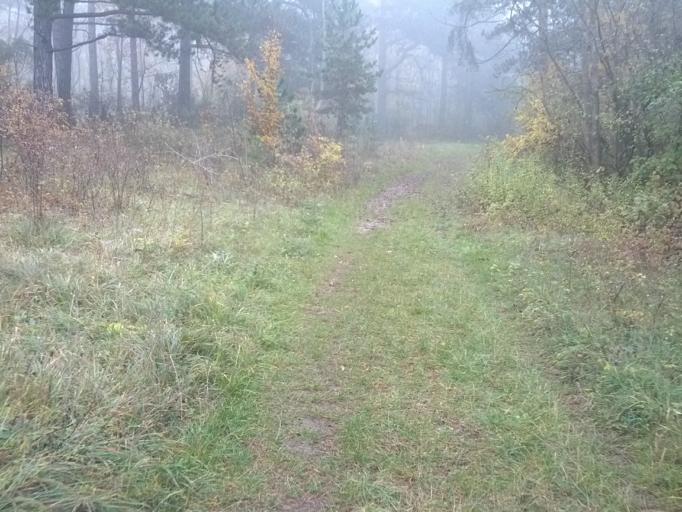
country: DE
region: Thuringia
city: Eisenach
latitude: 50.9742
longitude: 10.3535
